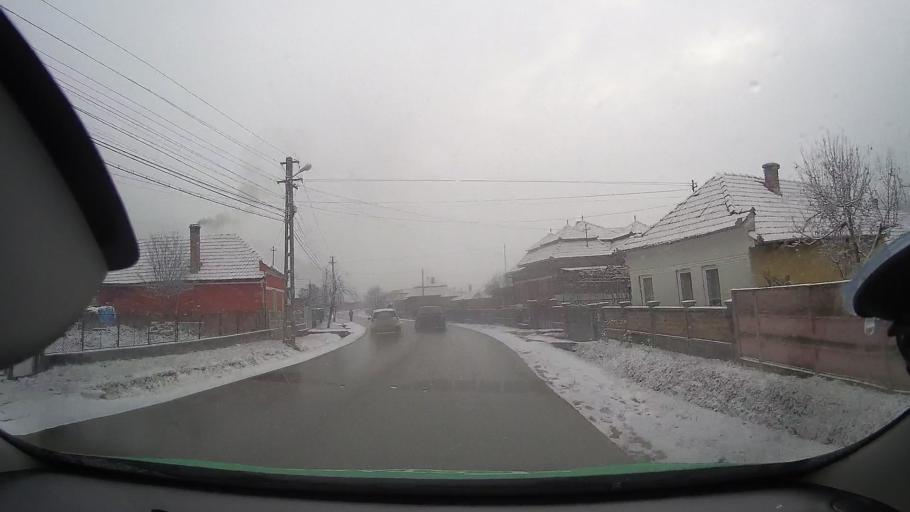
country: RO
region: Alba
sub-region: Comuna Lopadea Noua
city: Lopadea Noua
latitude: 46.3084
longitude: 23.7944
